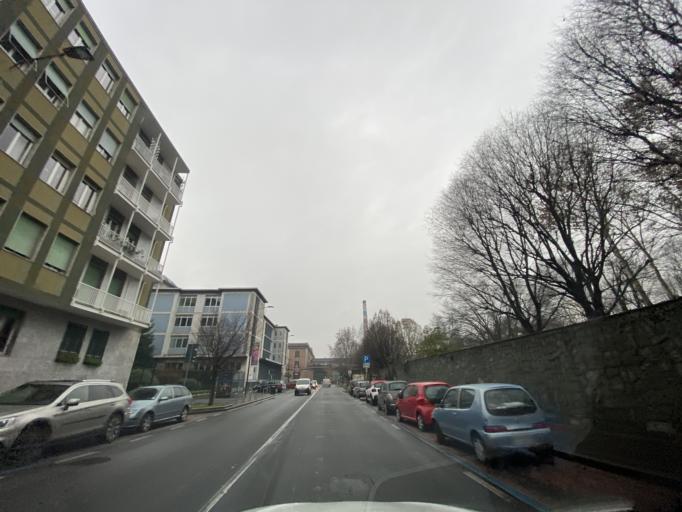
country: IT
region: Lombardy
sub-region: Citta metropolitana di Milano
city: Milano
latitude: 45.4980
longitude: 9.1786
